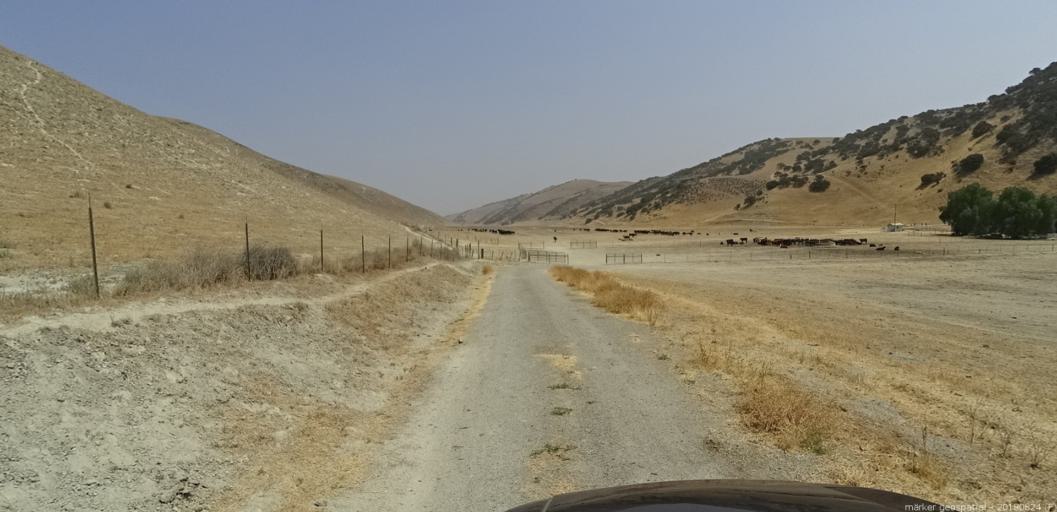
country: US
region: California
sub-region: Monterey County
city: King City
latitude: 36.2017
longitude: -120.9428
